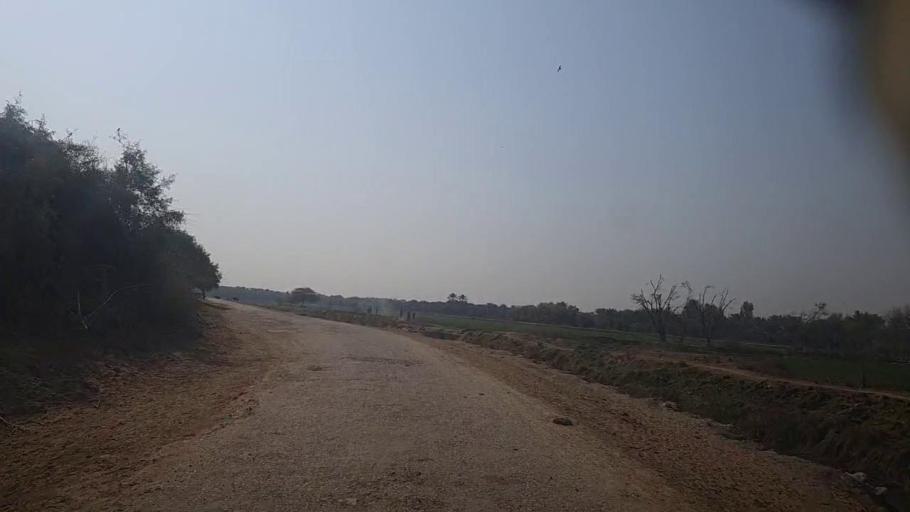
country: PK
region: Sindh
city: Kot Diji
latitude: 27.4040
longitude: 68.7798
